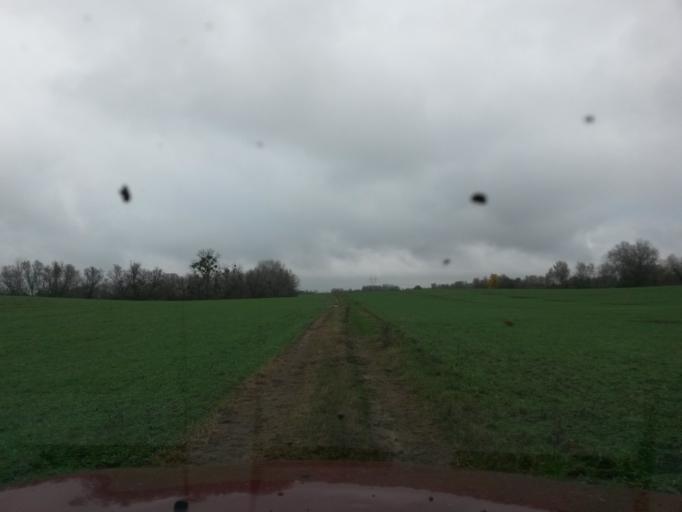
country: SK
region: Kosicky
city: Michalovce
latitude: 48.5535
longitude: 21.9331
